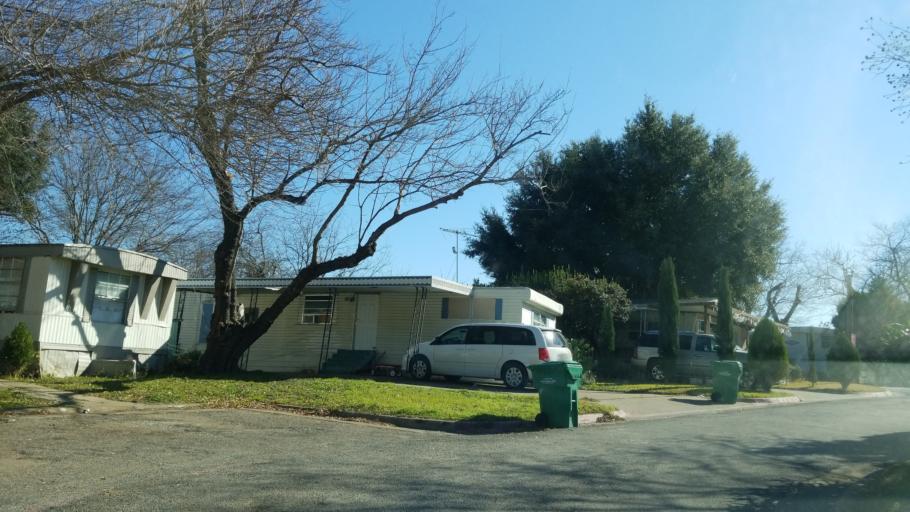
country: US
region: Texas
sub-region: Dallas County
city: Cockrell Hill
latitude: 32.7600
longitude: -96.9146
